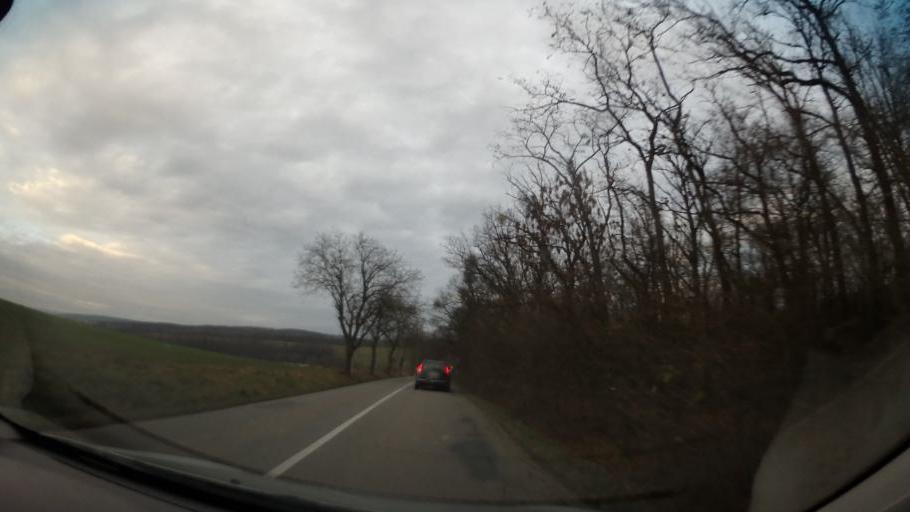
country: CZ
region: South Moravian
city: Ivancice
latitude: 49.1352
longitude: 16.3848
